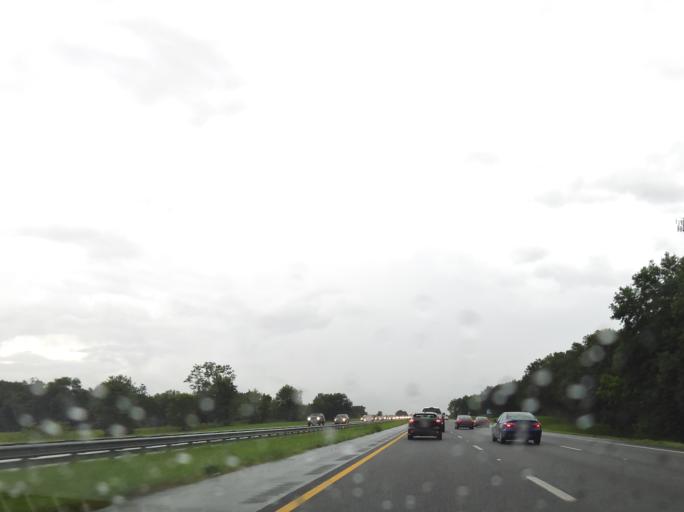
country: US
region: Florida
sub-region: Columbia County
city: Lake City
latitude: 30.0474
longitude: -82.6202
